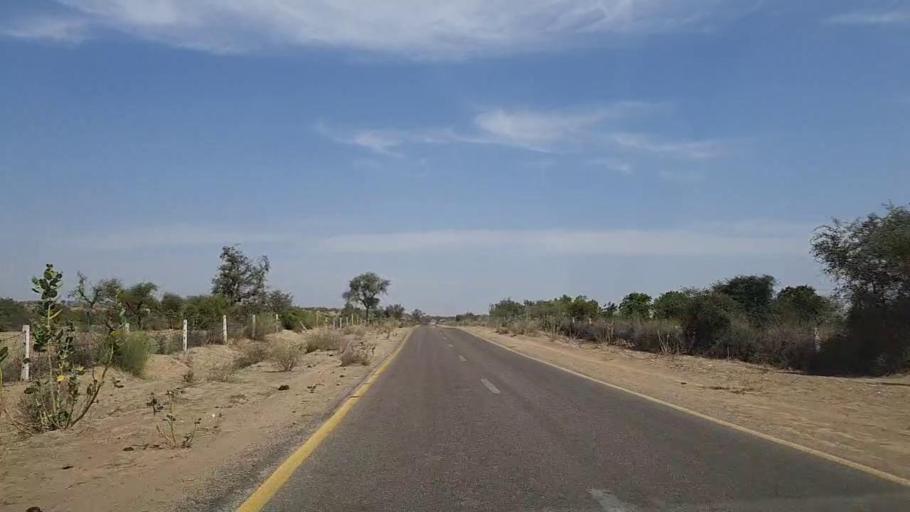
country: PK
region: Sindh
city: Mithi
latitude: 24.8229
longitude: 69.8242
